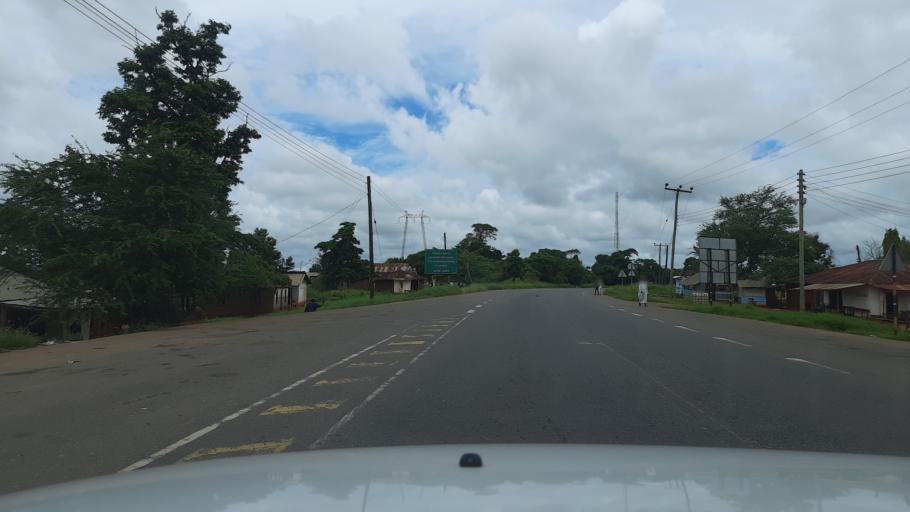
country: TZ
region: Tanga
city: Chanika
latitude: -5.9076
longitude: 38.2369
